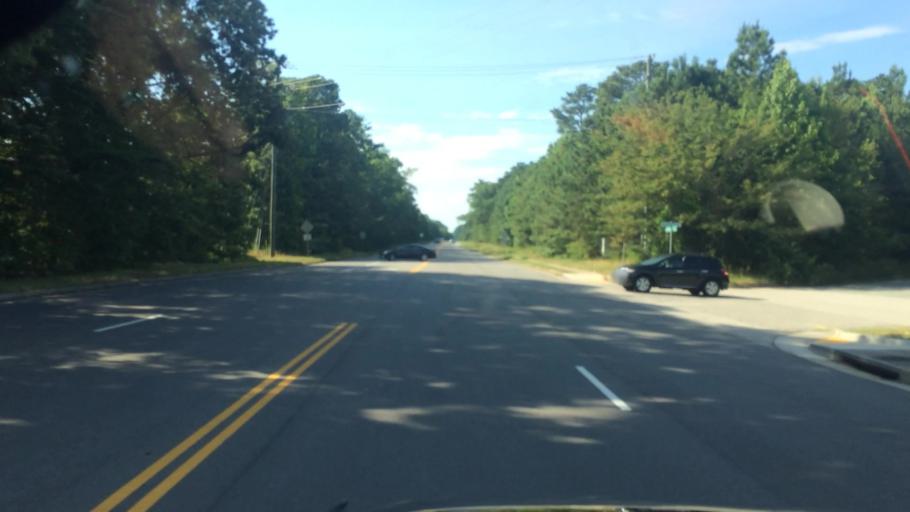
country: US
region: Virginia
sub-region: City of Williamsburg
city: Williamsburg
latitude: 37.2885
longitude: -76.7209
